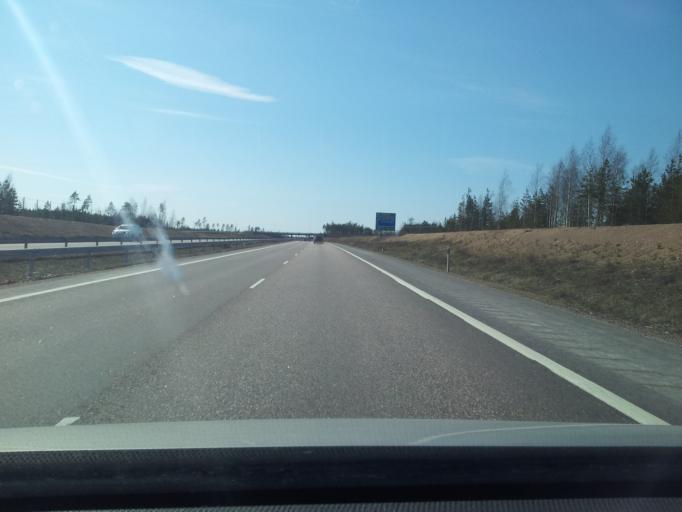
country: FI
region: Kymenlaakso
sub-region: Kotka-Hamina
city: Pyhtaeae
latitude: 60.4915
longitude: 26.5931
